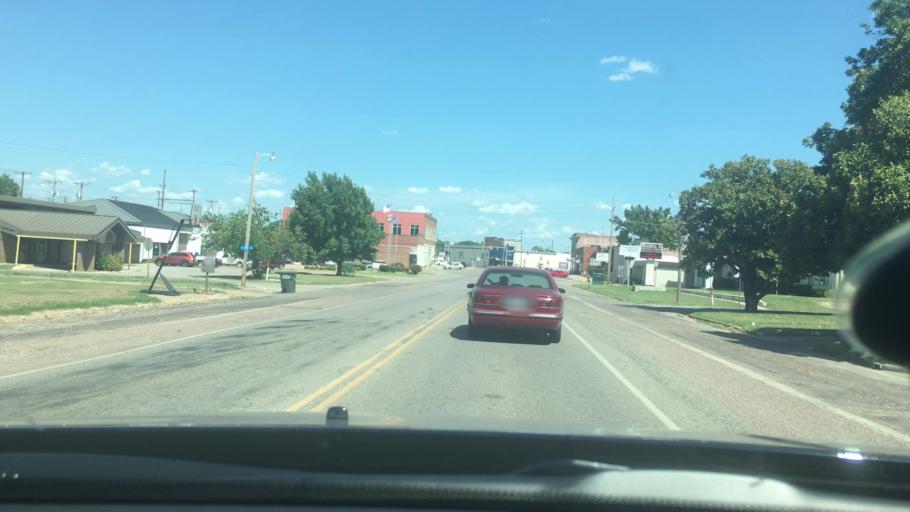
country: US
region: Oklahoma
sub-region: Marshall County
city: Madill
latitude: 34.0909
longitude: -96.7749
